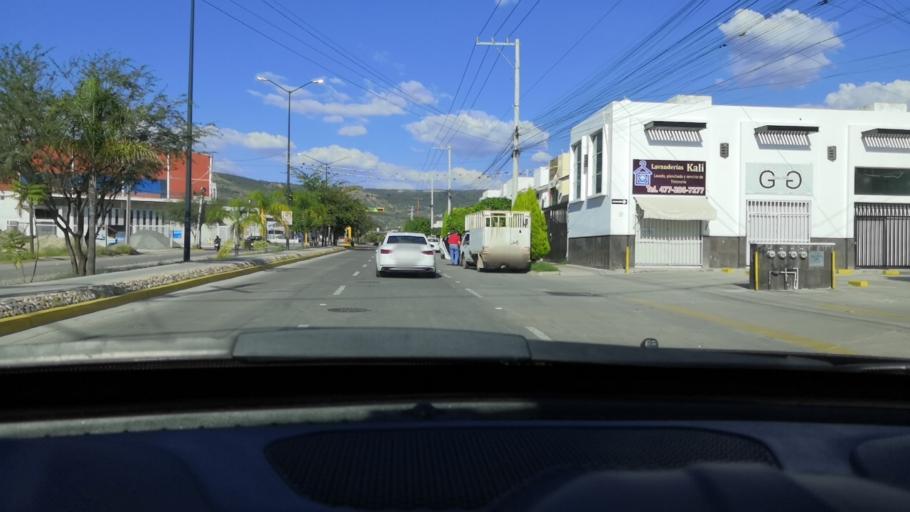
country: MX
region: Guanajuato
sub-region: Leon
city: Medina
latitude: 21.1664
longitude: -101.6460
